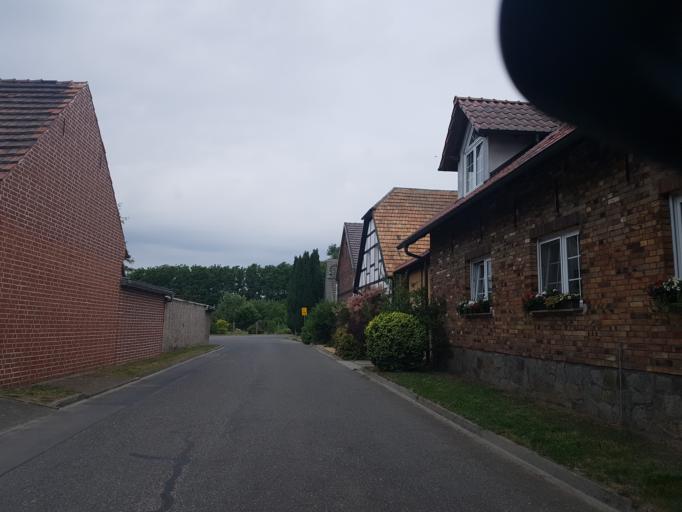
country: DE
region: Brandenburg
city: Doberlug-Kirchhain
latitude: 51.6919
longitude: 13.5153
